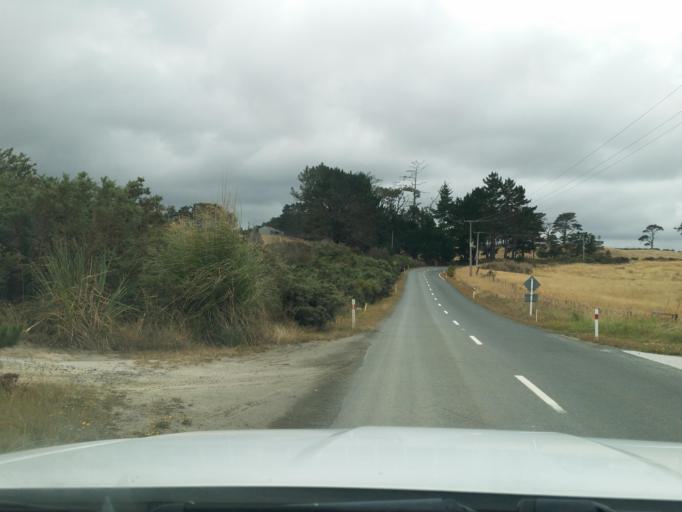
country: NZ
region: Northland
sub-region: Kaipara District
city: Dargaville
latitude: -35.9706
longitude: 173.8241
